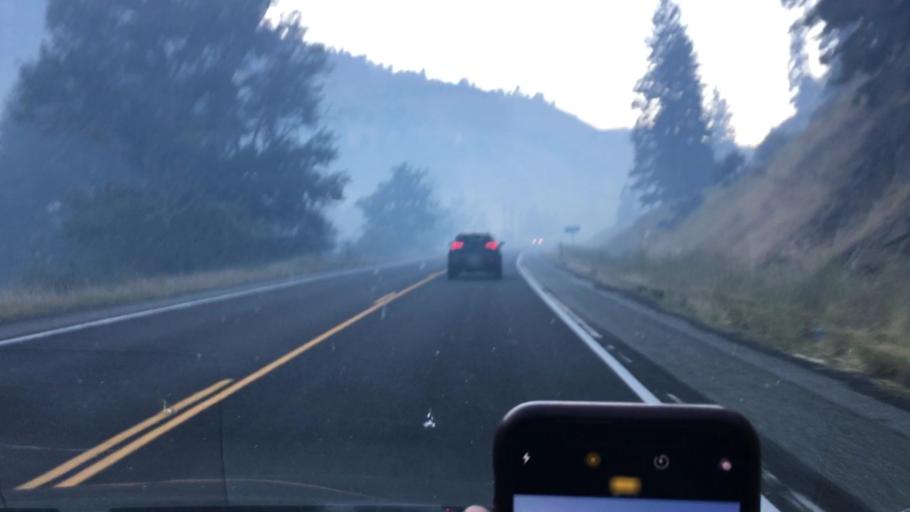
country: US
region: Idaho
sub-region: Valley County
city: McCall
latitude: 45.2859
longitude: -116.3526
